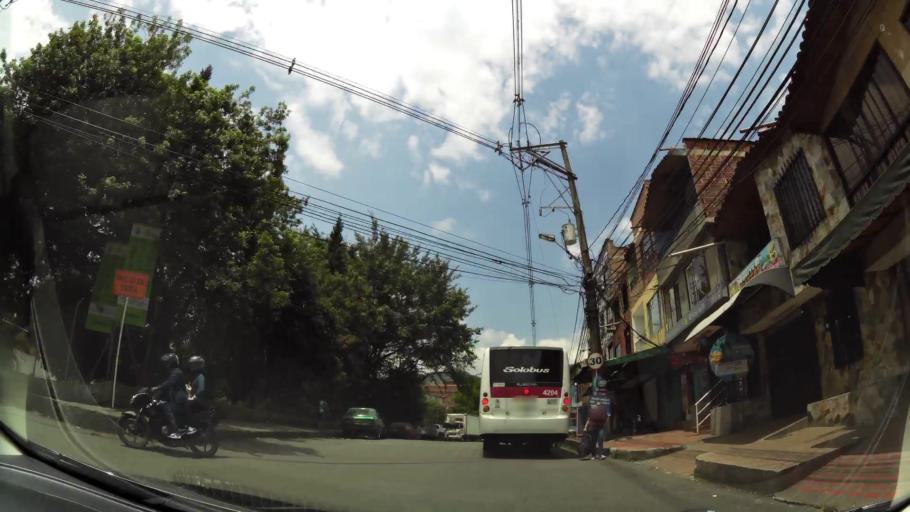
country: CO
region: Antioquia
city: Itagui
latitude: 6.1816
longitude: -75.6047
